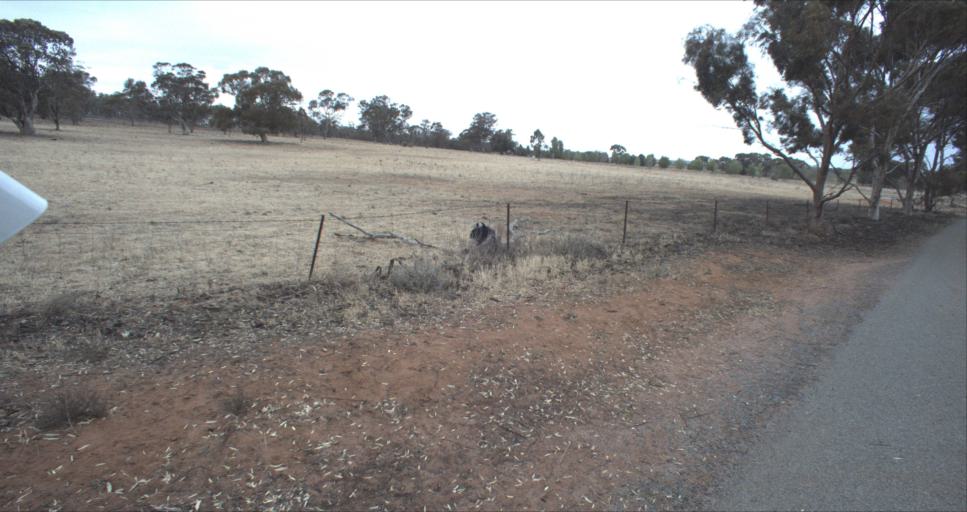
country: AU
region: New South Wales
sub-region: Leeton
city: Leeton
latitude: -34.4516
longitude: 146.3942
